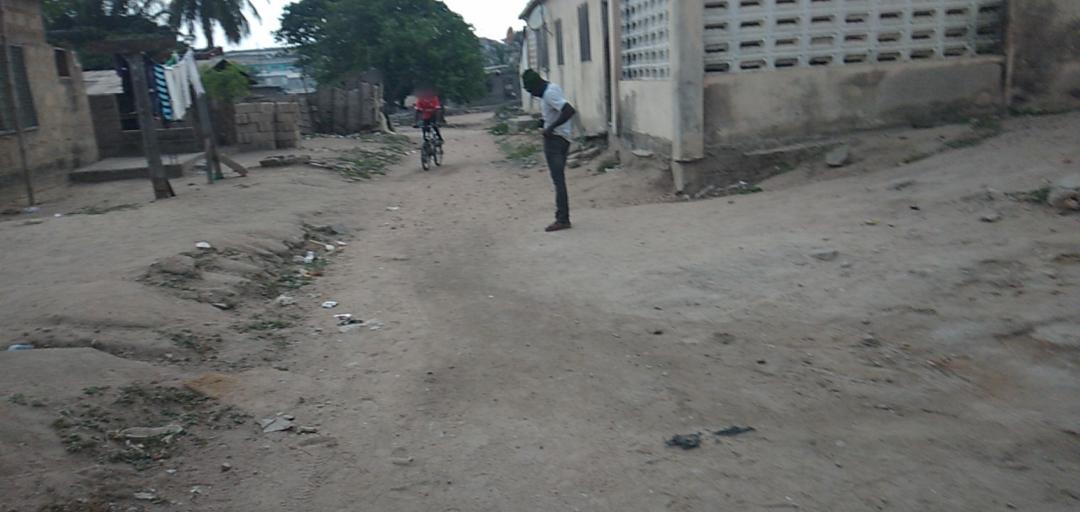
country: GH
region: Central
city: Winneba
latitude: 5.3498
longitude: -0.6148
